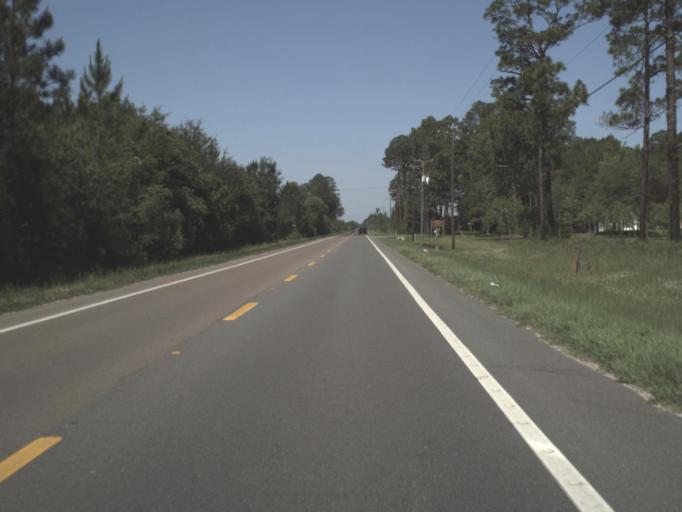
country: US
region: Florida
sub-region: Baker County
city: Macclenny
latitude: 30.2715
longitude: -82.1839
